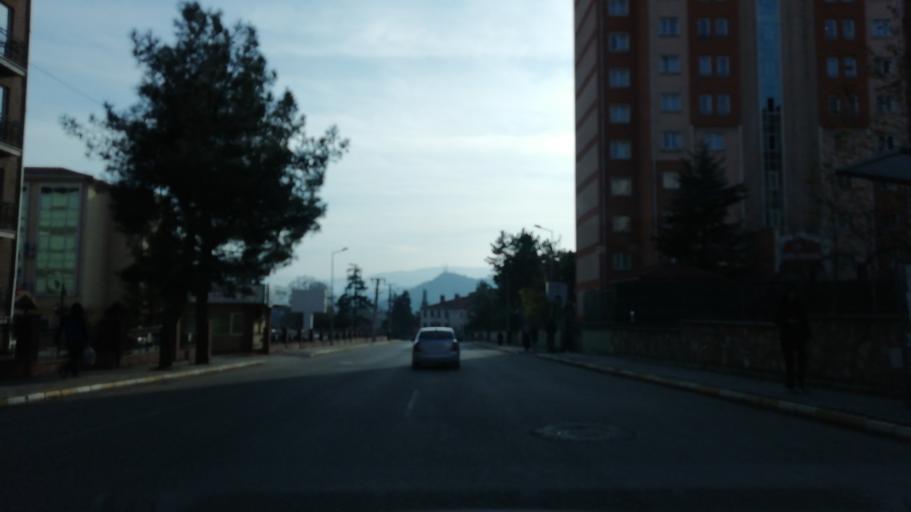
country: TR
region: Karabuk
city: Karabuk
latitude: 41.2024
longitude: 32.6265
